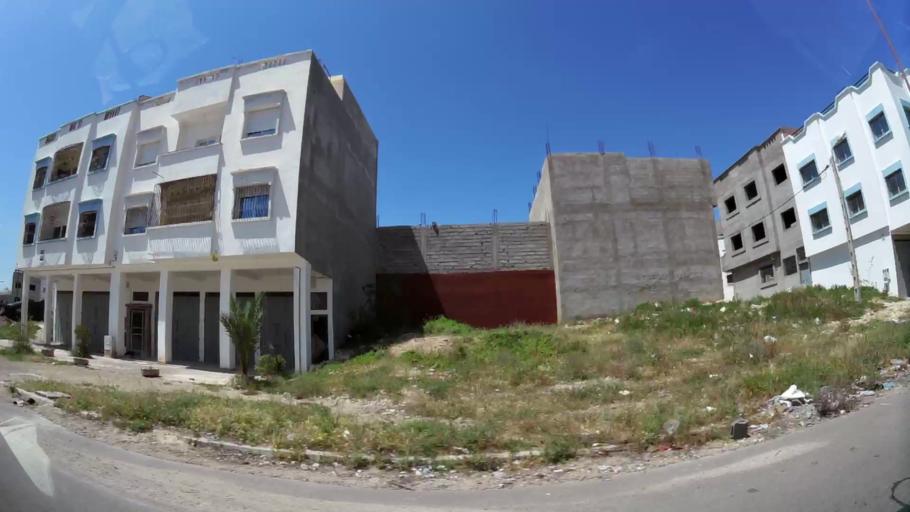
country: MA
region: Oued ed Dahab-Lagouira
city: Dakhla
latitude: 30.4273
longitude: -9.5523
